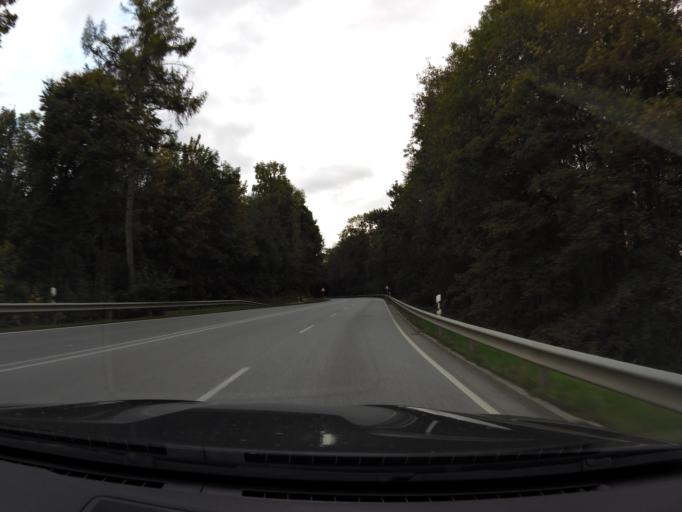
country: DE
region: Bavaria
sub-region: Lower Bavaria
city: Kumhausen
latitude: 48.4807
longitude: 12.1575
